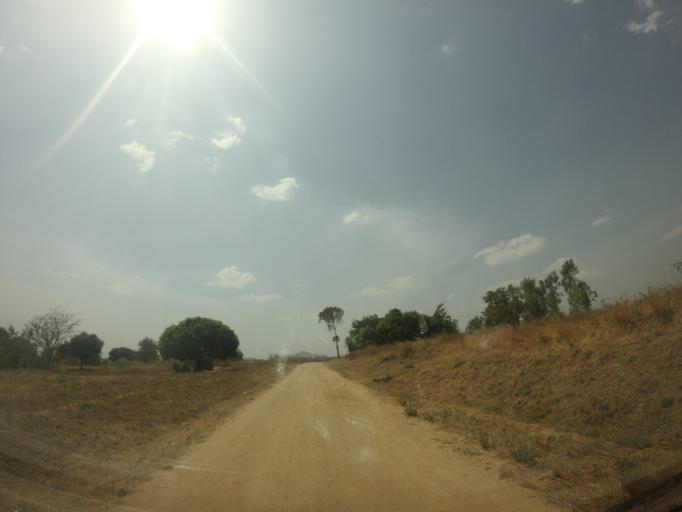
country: UG
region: Northern Region
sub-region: Arua District
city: Arua
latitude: 2.9124
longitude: 31.0461
